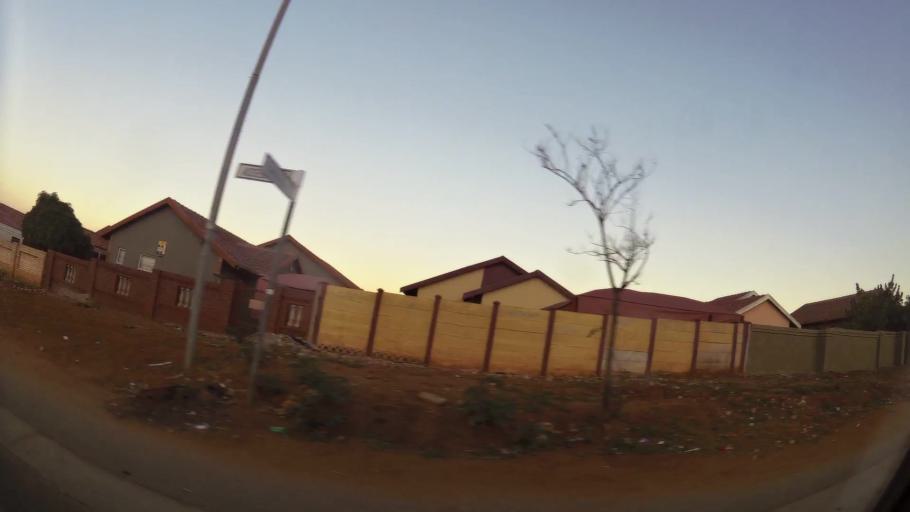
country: ZA
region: North-West
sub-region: Bojanala Platinum District Municipality
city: Rustenburg
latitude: -25.6500
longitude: 27.2056
